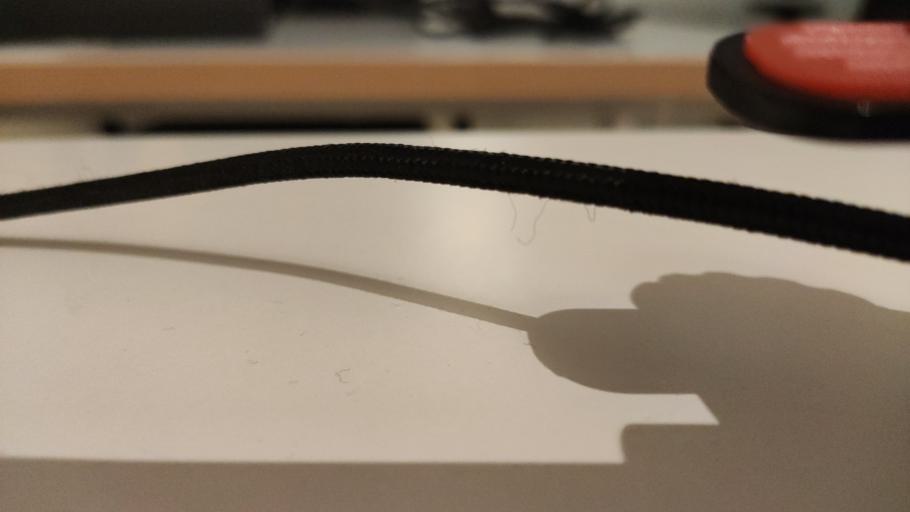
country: RU
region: Moskovskaya
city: Shaburnovo
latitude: 56.4358
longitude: 37.9220
